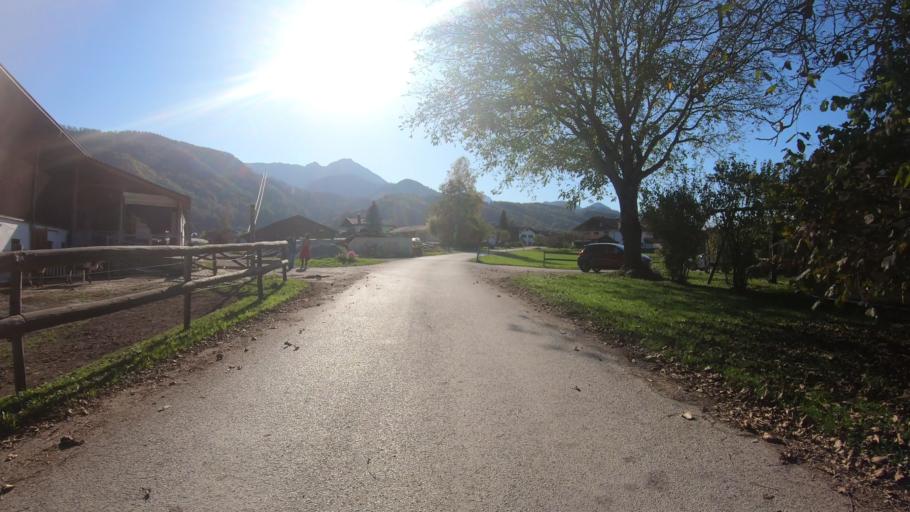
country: DE
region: Bavaria
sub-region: Upper Bavaria
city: Bergen
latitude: 47.8044
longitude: 12.5945
